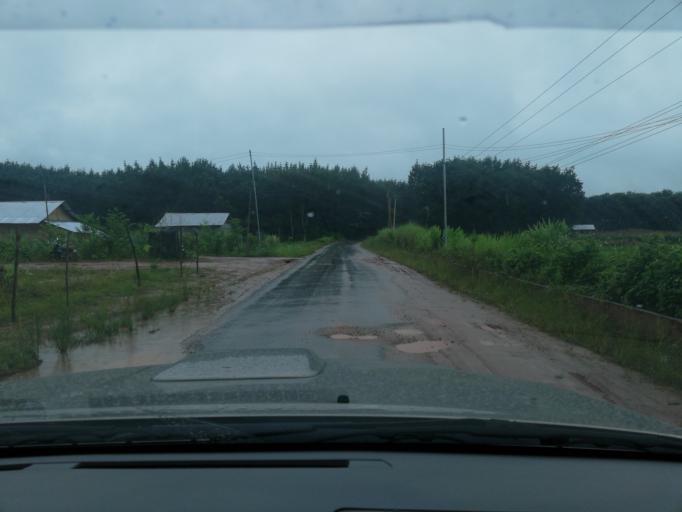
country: LA
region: Loungnamtha
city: Louang Namtha
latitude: 20.9772
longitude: 101.3847
